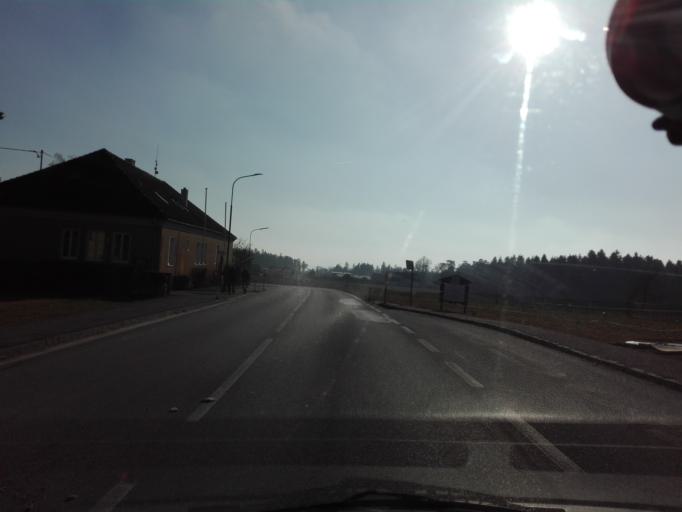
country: AT
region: Upper Austria
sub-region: Politischer Bezirk Urfahr-Umgebung
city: Engerwitzdorf
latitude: 48.3129
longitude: 14.5401
